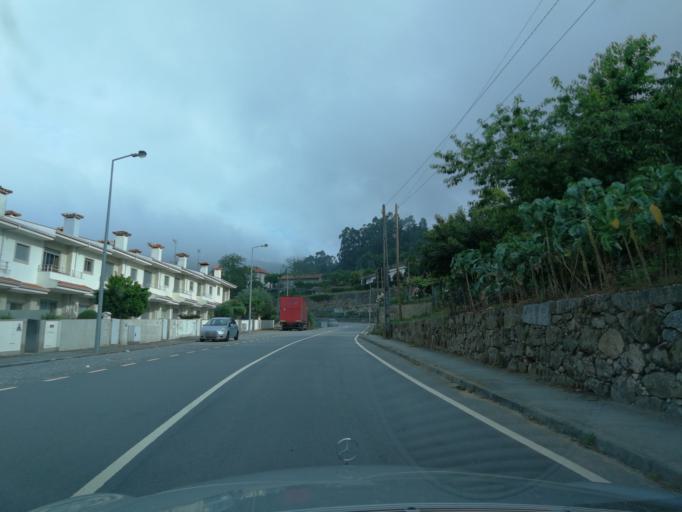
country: PT
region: Braga
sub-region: Guimaraes
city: Ponte
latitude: 41.5184
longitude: -8.3577
